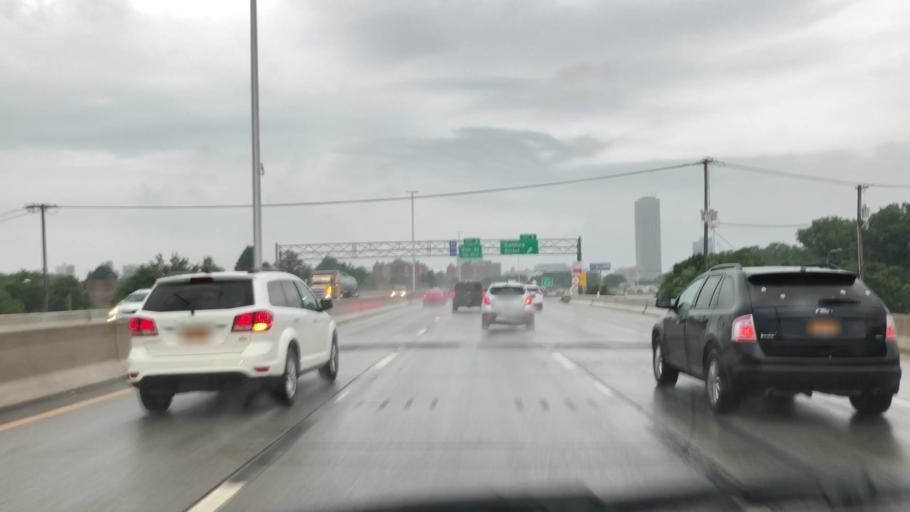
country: US
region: New York
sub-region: Erie County
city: Buffalo
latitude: 42.8733
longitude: -78.8564
